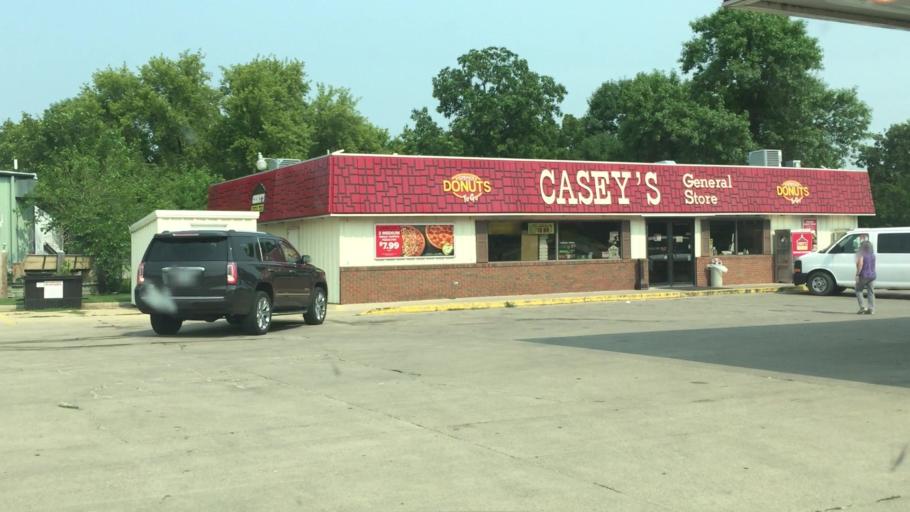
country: US
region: Iowa
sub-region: Dickinson County
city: Arnolds Park
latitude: 43.3629
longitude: -95.1392
